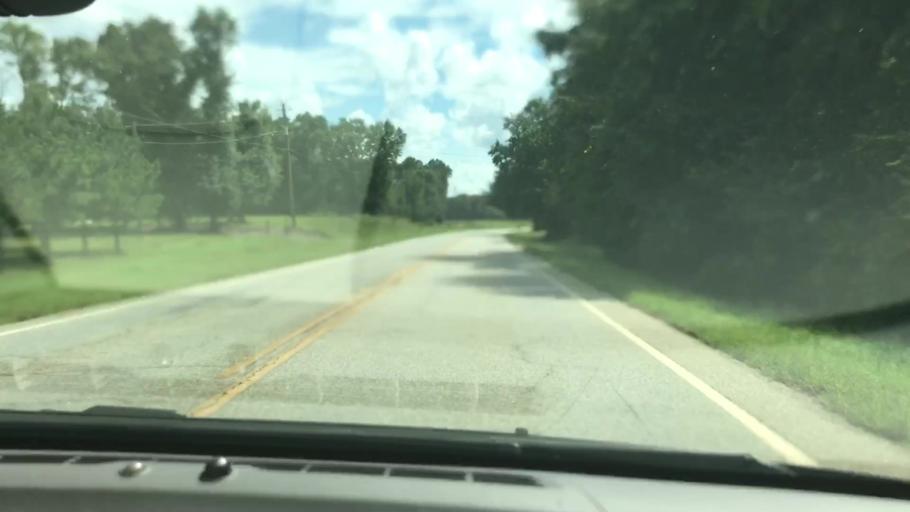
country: US
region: Georgia
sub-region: Clay County
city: Fort Gaines
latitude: 31.7060
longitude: -85.0417
